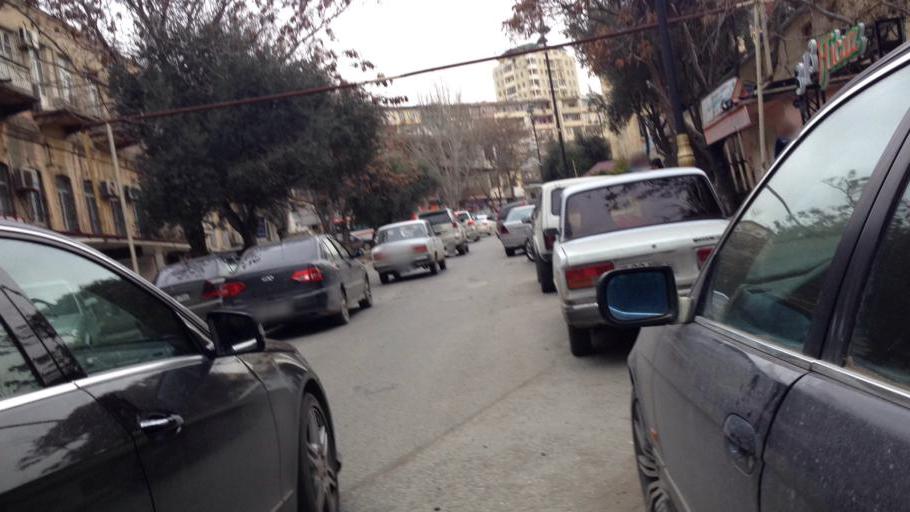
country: AZ
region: Baki
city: Baku
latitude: 40.3876
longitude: 49.8519
